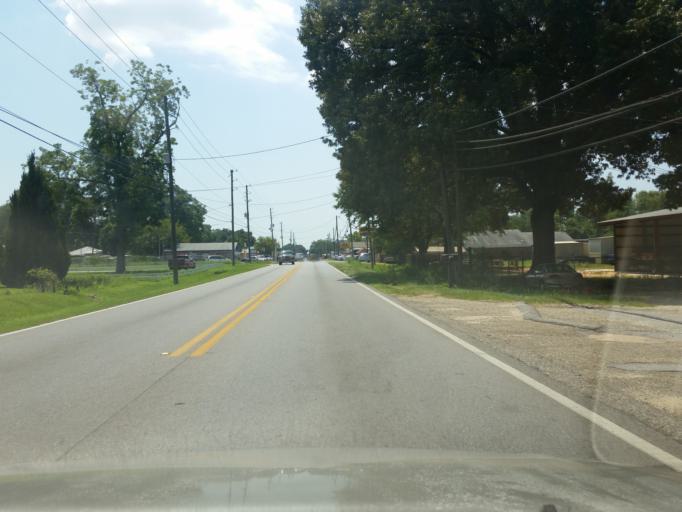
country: US
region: Florida
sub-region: Escambia County
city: Ensley
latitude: 30.5252
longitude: -87.2696
